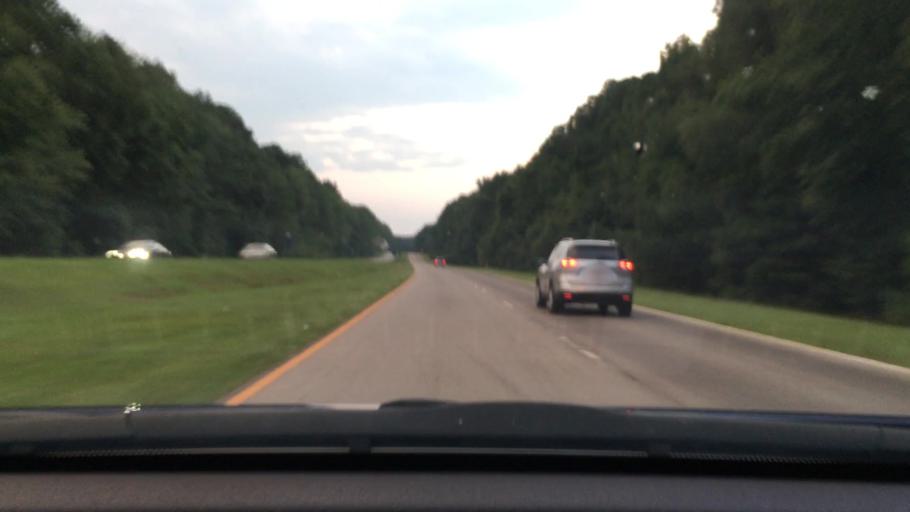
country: US
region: South Carolina
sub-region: Sumter County
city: Stateburg
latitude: 33.9464
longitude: -80.6366
